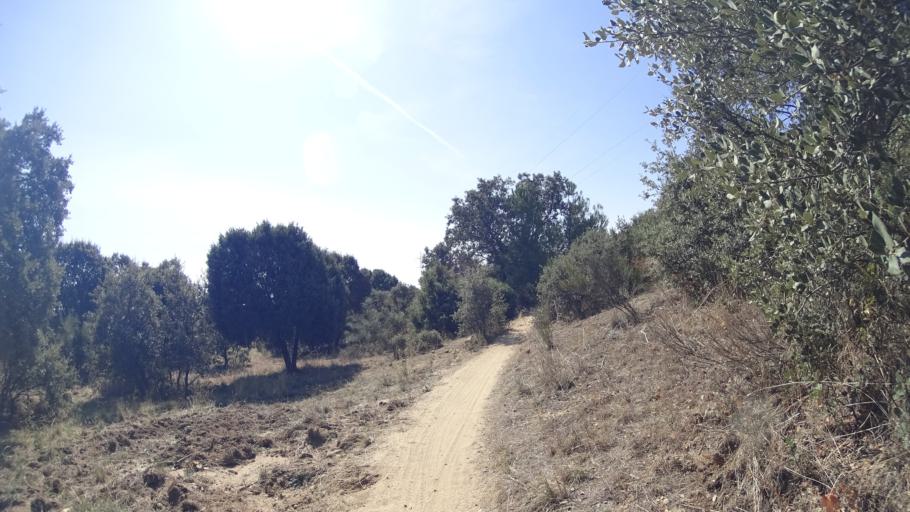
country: ES
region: Madrid
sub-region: Provincia de Madrid
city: Colmenarejo
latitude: 40.5713
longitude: -4.0249
